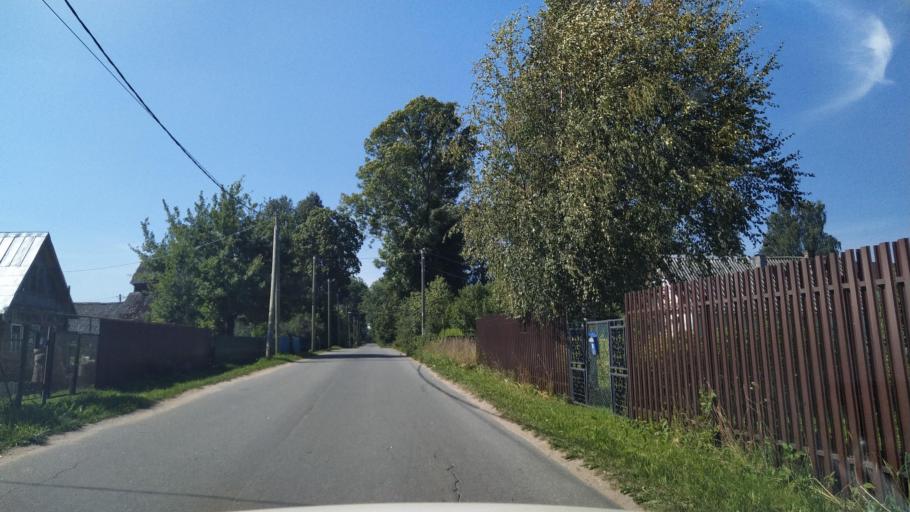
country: RU
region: Leningrad
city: Siverskiy
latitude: 59.2647
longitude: 30.0409
